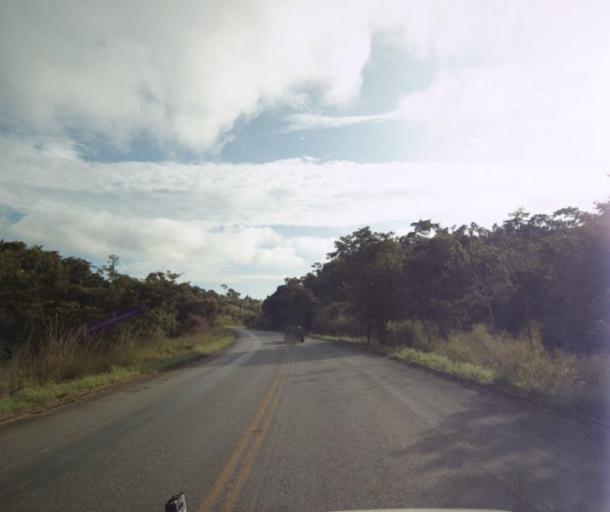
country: BR
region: Goias
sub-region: Pirenopolis
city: Pirenopolis
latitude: -15.7134
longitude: -48.6945
